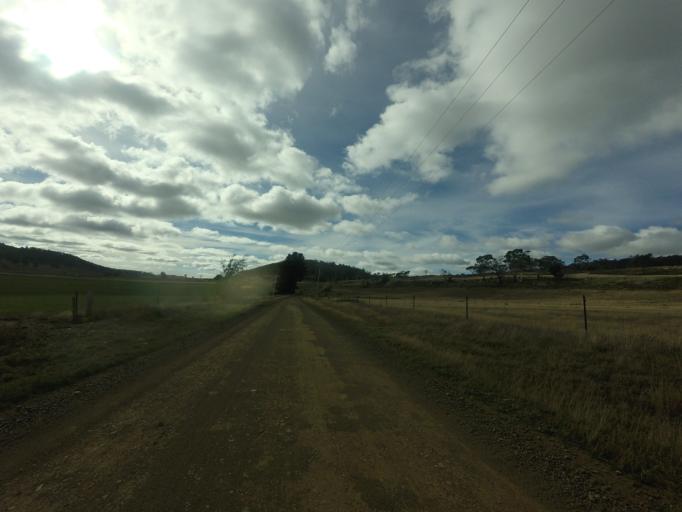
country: AU
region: Tasmania
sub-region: Brighton
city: Bridgewater
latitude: -42.3920
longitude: 147.3978
